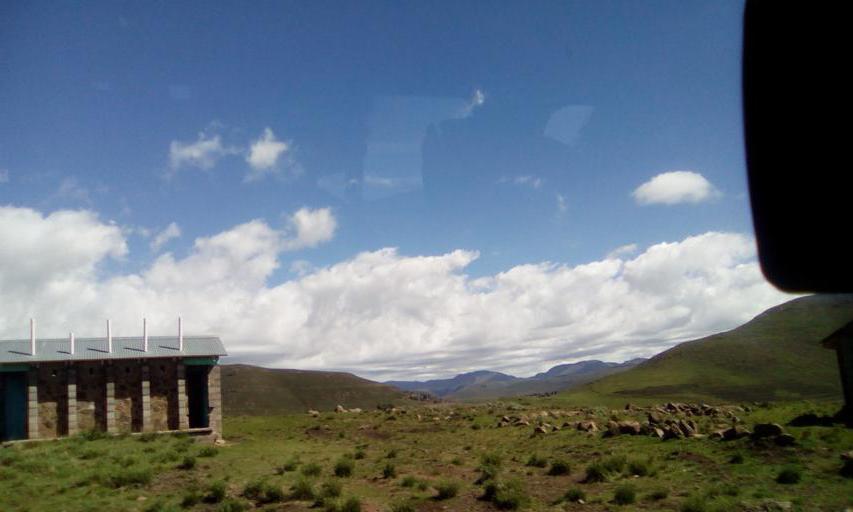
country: LS
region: Maseru
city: Nako
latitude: -29.8175
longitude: 28.0352
